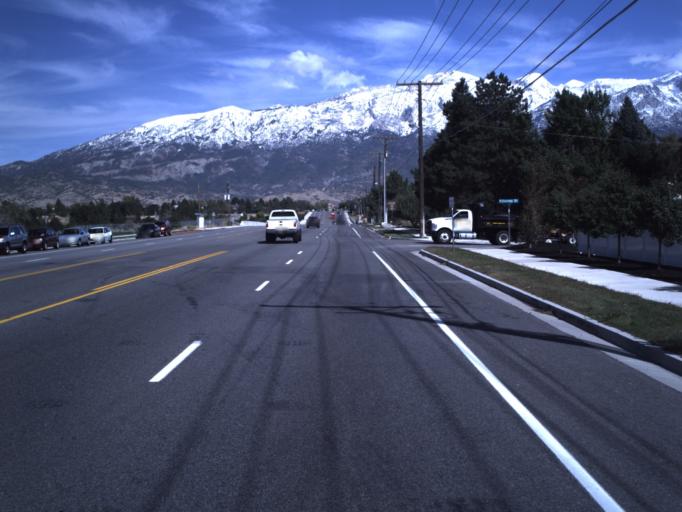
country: US
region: Utah
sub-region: Utah County
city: Cedar Hills
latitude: 40.4213
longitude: -111.7734
